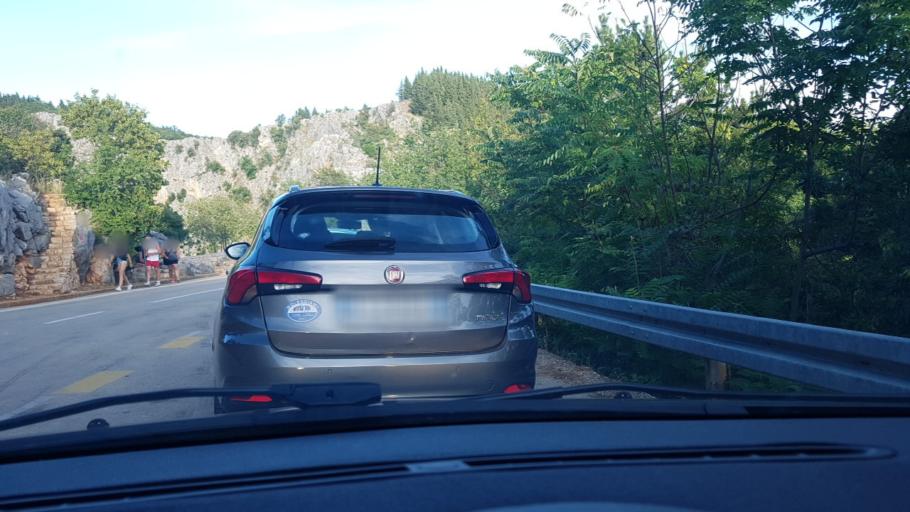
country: HR
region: Splitsko-Dalmatinska
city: Imotski
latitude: 43.4537
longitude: 17.1964
